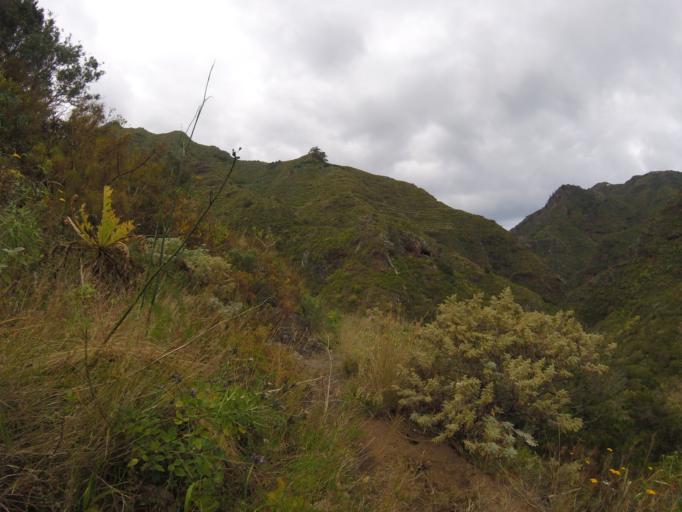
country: ES
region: Canary Islands
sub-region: Provincia de Santa Cruz de Tenerife
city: Tegueste
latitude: 28.5503
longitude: -16.2917
